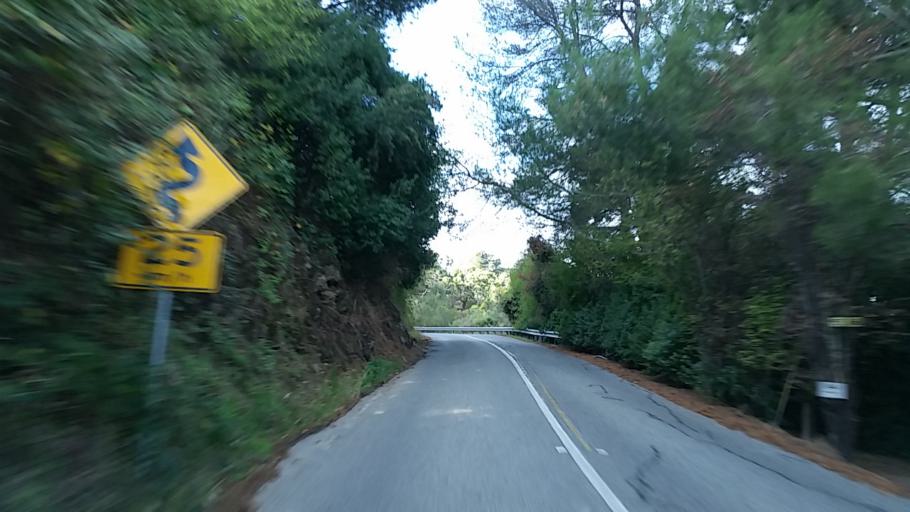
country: AU
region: South Australia
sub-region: Adelaide Hills
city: Adelaide Hills
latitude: -34.8896
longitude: 138.7411
